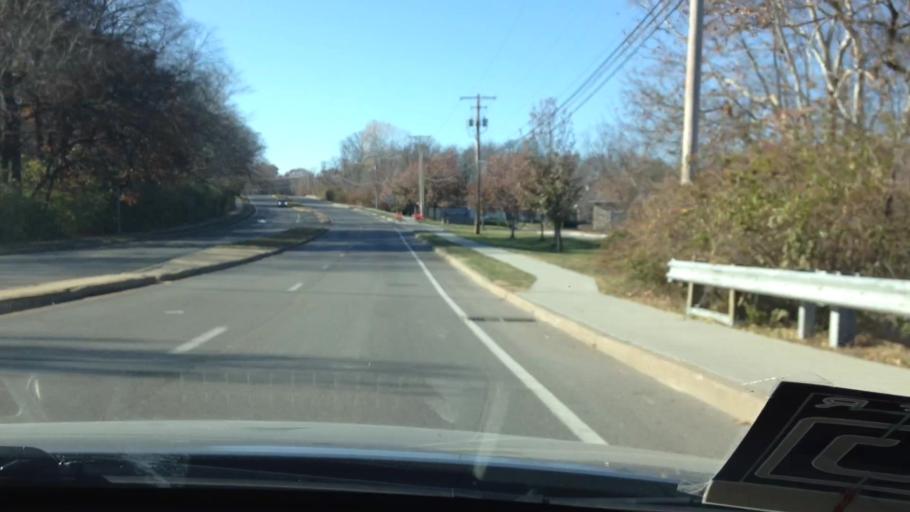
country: US
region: Kansas
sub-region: Johnson County
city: Leawood
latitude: 38.9557
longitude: -94.5839
